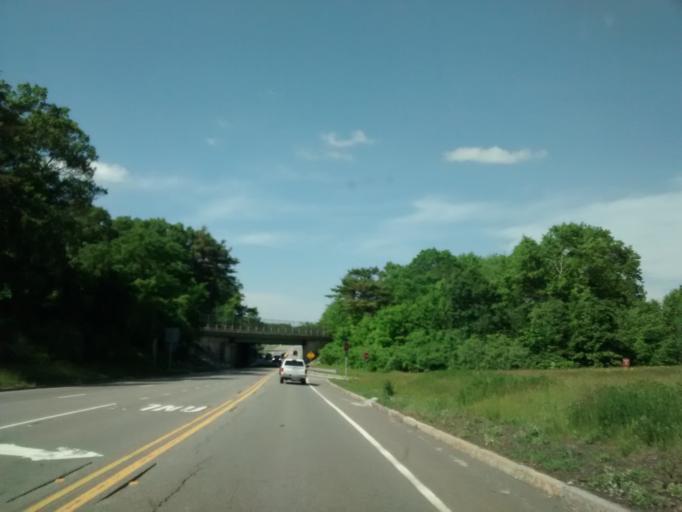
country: US
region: Massachusetts
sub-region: Worcester County
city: Shrewsbury
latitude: 42.2815
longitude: -71.6707
